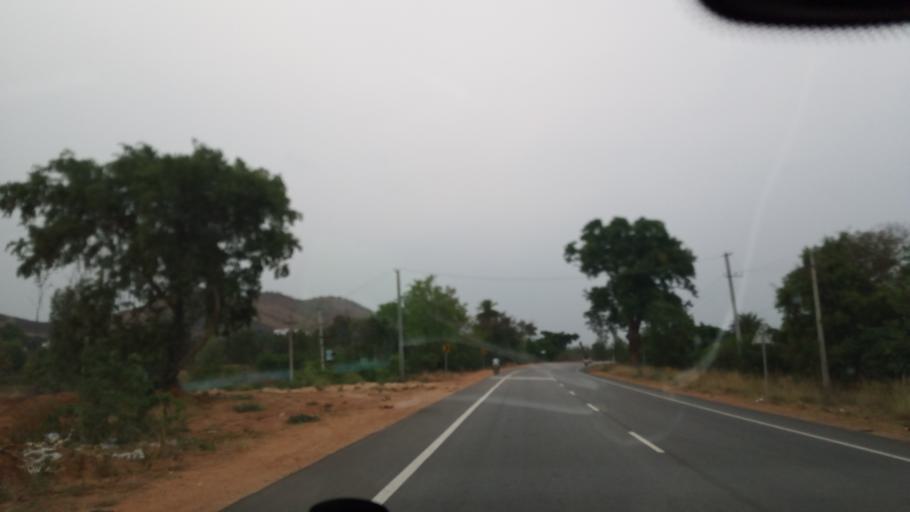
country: IN
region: Karnataka
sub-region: Mandya
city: Nagamangala
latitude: 12.7758
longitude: 76.7414
